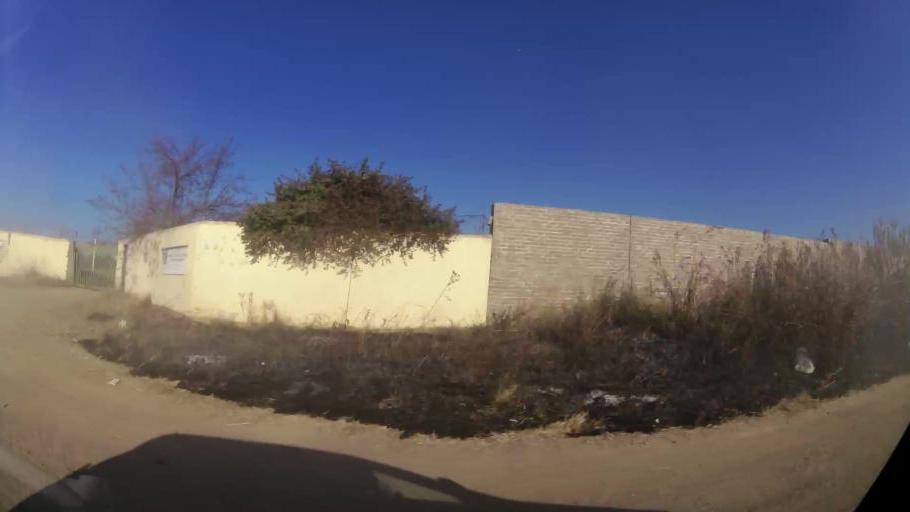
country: ZA
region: Gauteng
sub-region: West Rand District Municipality
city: Muldersdriseloop
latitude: -26.0233
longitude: 27.8744
